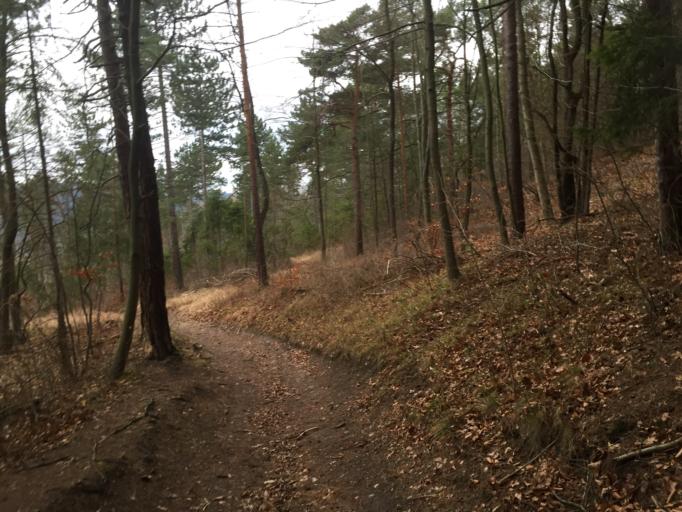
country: DE
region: Thuringia
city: Bad Blankenburg
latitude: 50.6936
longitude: 11.2722
